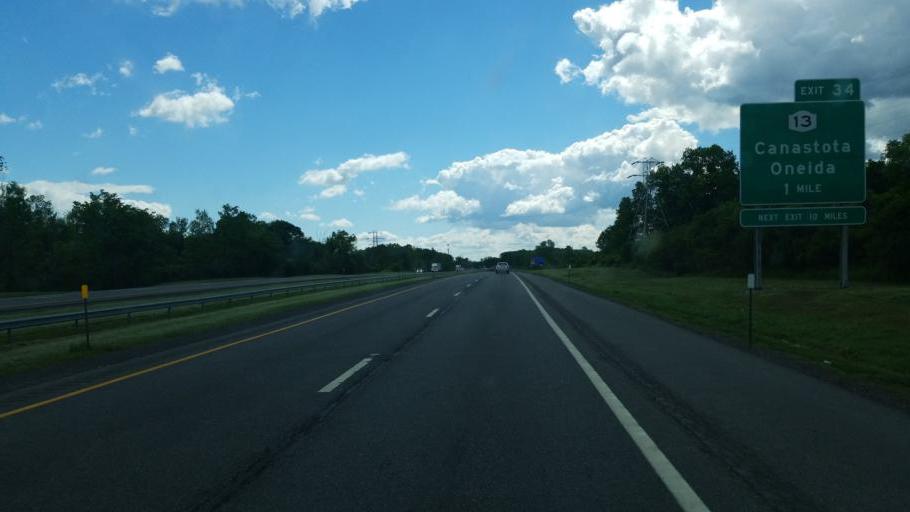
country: US
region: New York
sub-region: Madison County
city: Canastota
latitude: 43.0911
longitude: -75.7754
